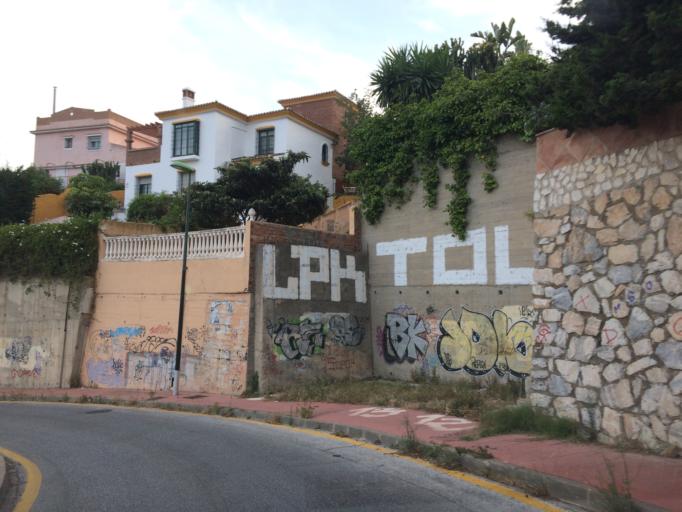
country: ES
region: Andalusia
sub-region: Provincia de Malaga
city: Malaga
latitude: 36.7295
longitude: -4.3861
